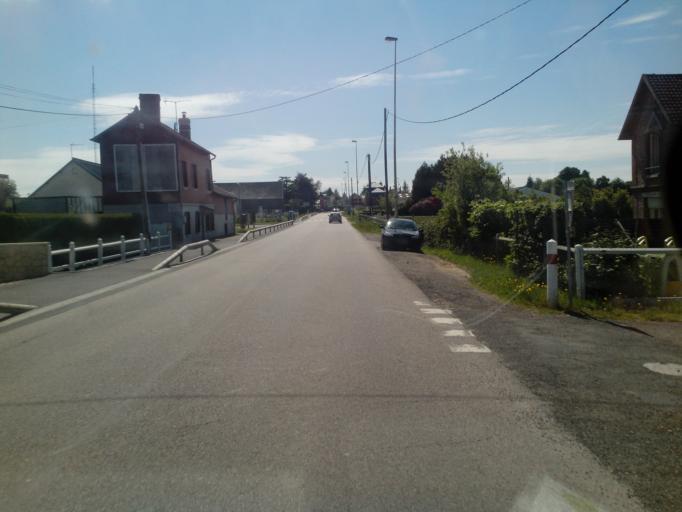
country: FR
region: Haute-Normandie
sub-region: Departement de l'Eure
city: Beuzeville
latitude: 49.3461
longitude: 0.3540
